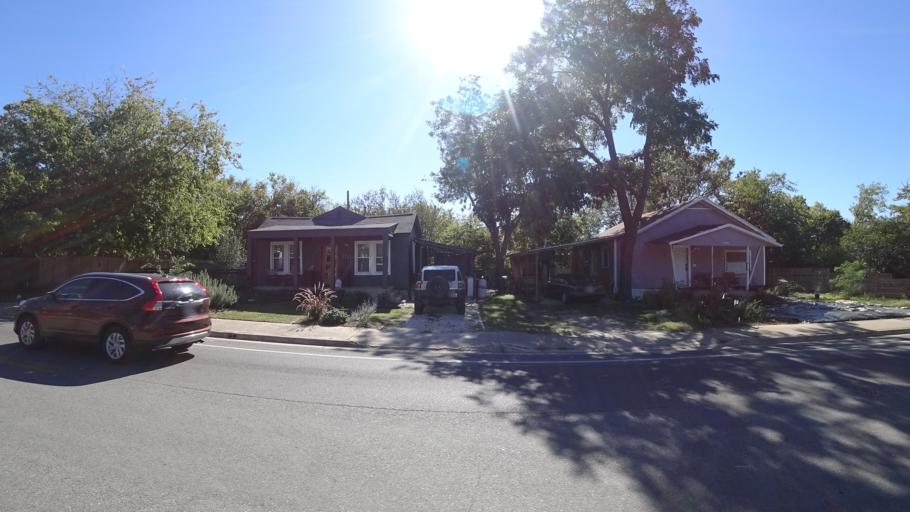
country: US
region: Texas
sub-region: Travis County
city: Austin
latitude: 30.3238
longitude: -97.7349
